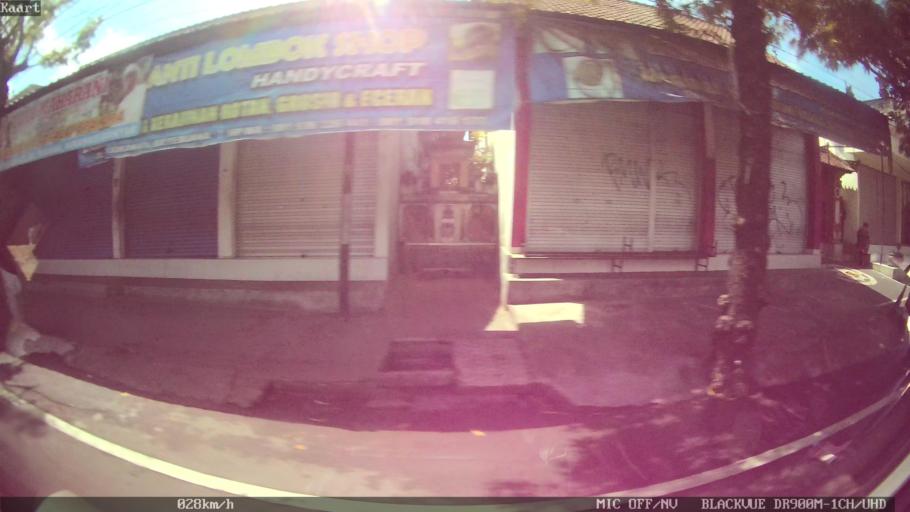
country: ID
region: Bali
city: Banjar Pasekan
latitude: -8.6005
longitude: 115.2831
